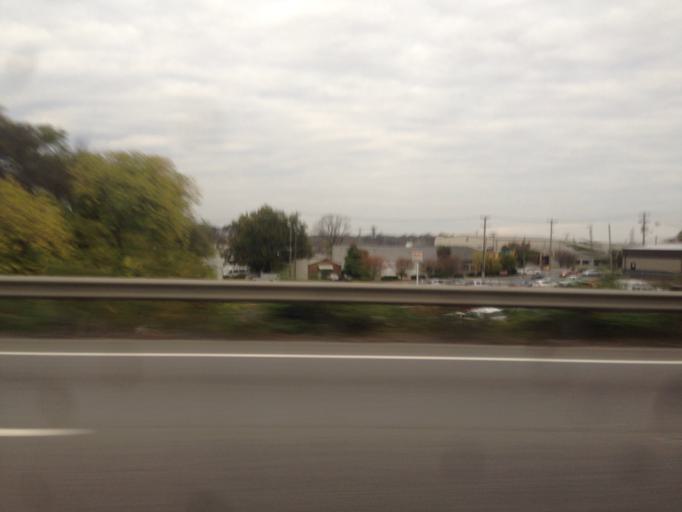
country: US
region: Tennessee
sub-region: Davidson County
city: Nashville
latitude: 36.1527
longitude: -86.7546
